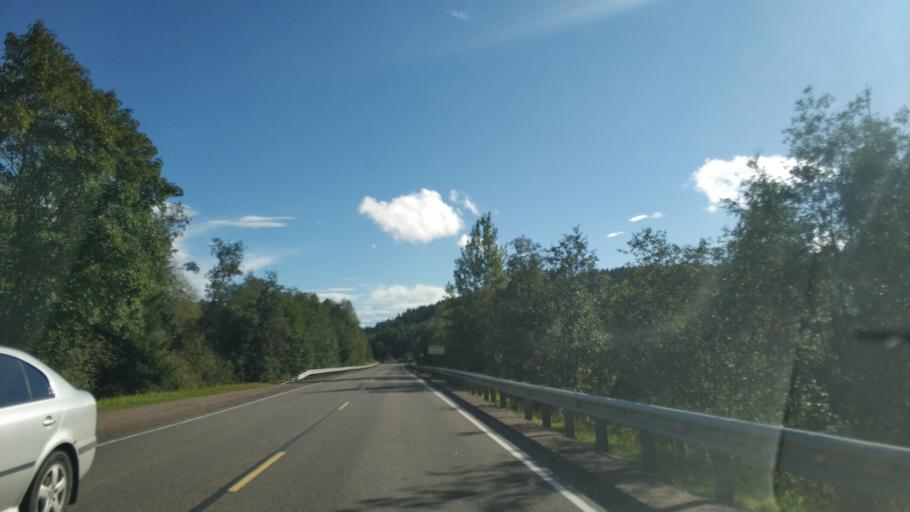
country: RU
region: Republic of Karelia
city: Sortavala
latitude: 61.6703
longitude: 30.6540
